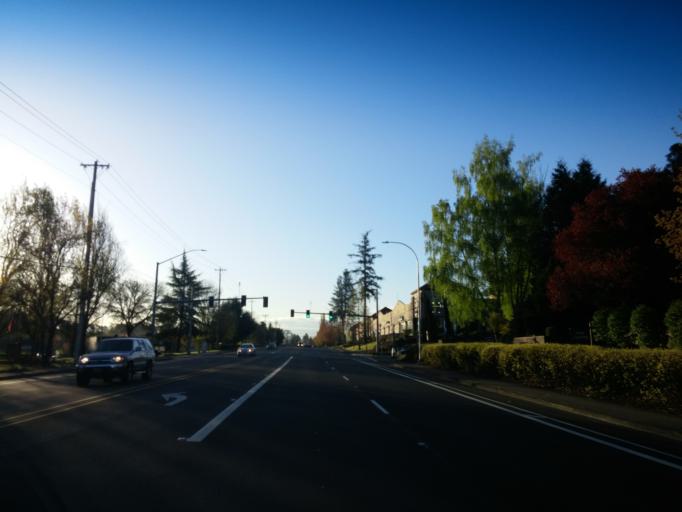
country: US
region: Oregon
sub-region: Washington County
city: Oak Hills
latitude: 45.5185
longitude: -122.8449
